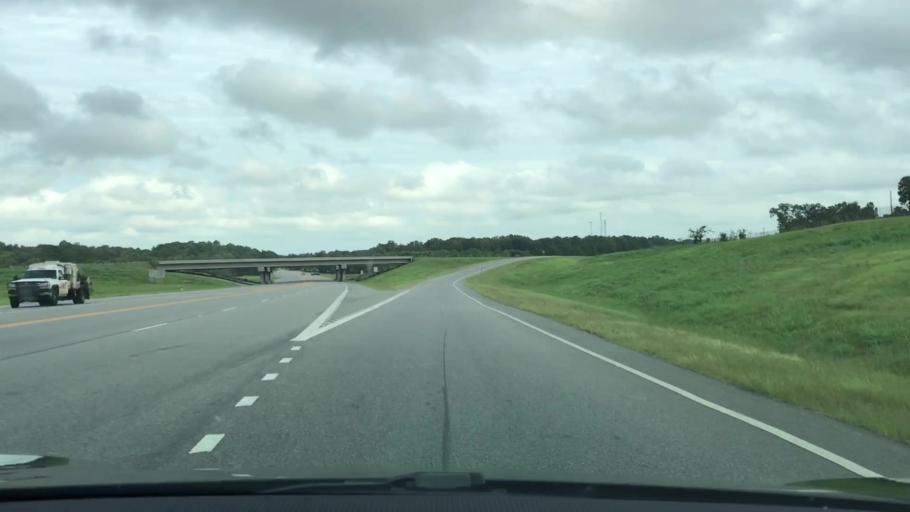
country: US
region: Alabama
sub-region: Montgomery County
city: Pike Road
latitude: 32.3365
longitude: -86.0609
